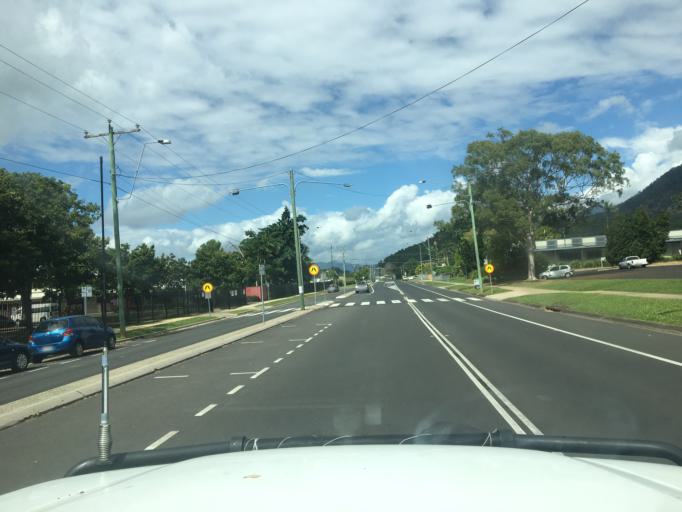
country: AU
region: Queensland
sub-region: Cairns
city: Woree
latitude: -16.9605
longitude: 145.7403
